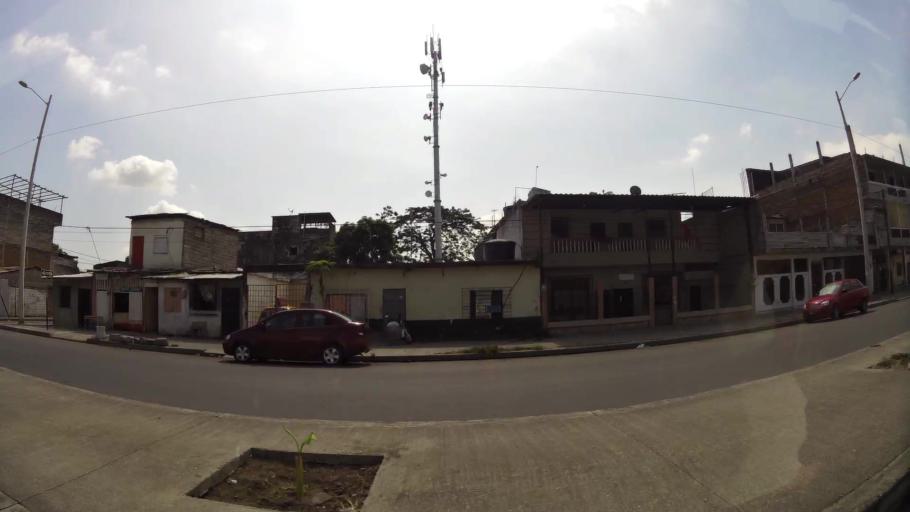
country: EC
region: Guayas
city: Eloy Alfaro
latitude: -2.1646
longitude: -79.8382
